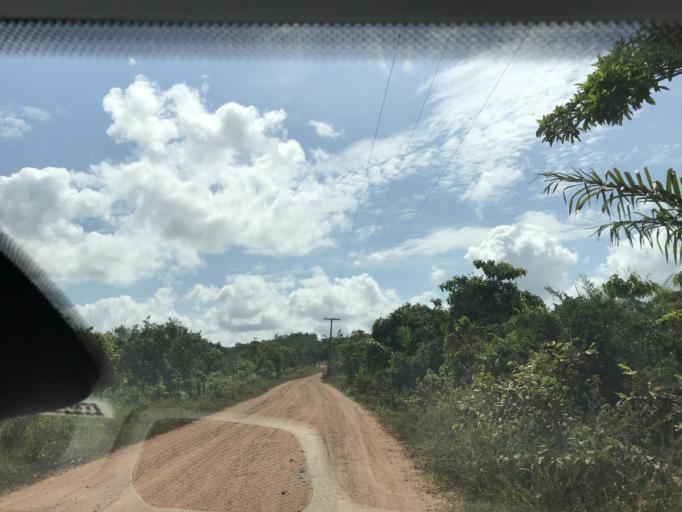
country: BR
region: Bahia
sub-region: Entre Rios
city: Entre Rios
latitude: -12.1870
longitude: -38.0508
